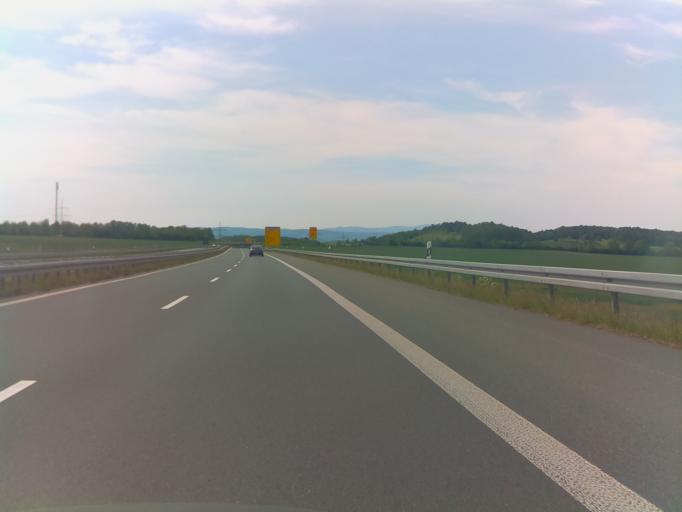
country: DE
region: Saxony-Anhalt
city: Quedlinburg
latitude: 51.8148
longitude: 11.1466
